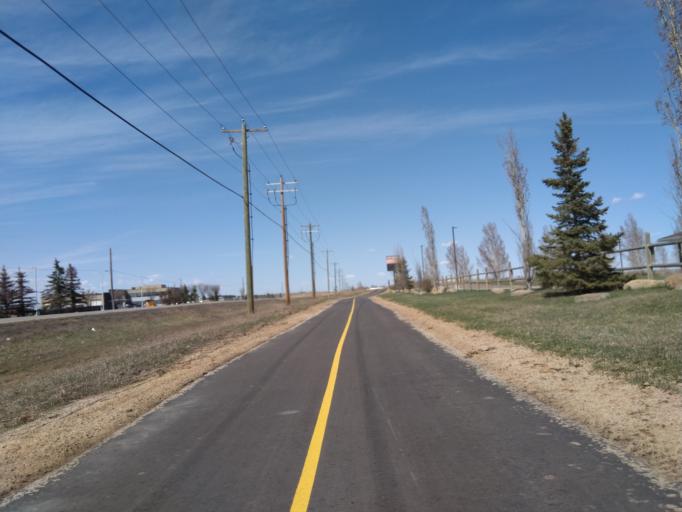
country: CA
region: Alberta
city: Chestermere
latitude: 50.9545
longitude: -113.9116
